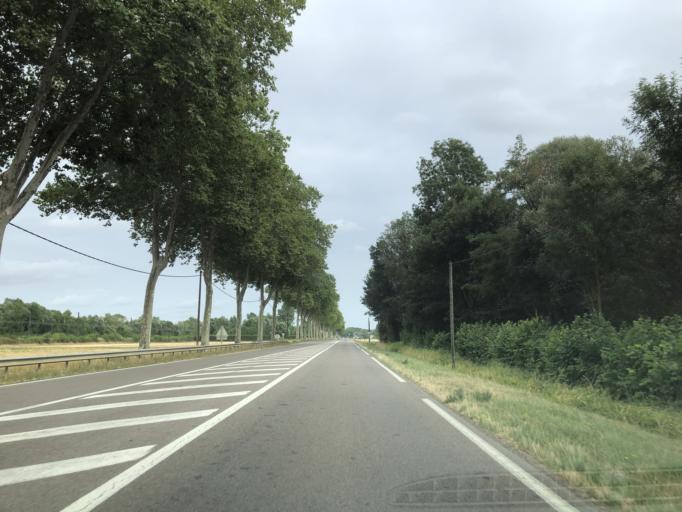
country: FR
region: Bourgogne
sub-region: Departement de l'Yonne
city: Joigny
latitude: 47.9632
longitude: 3.4320
